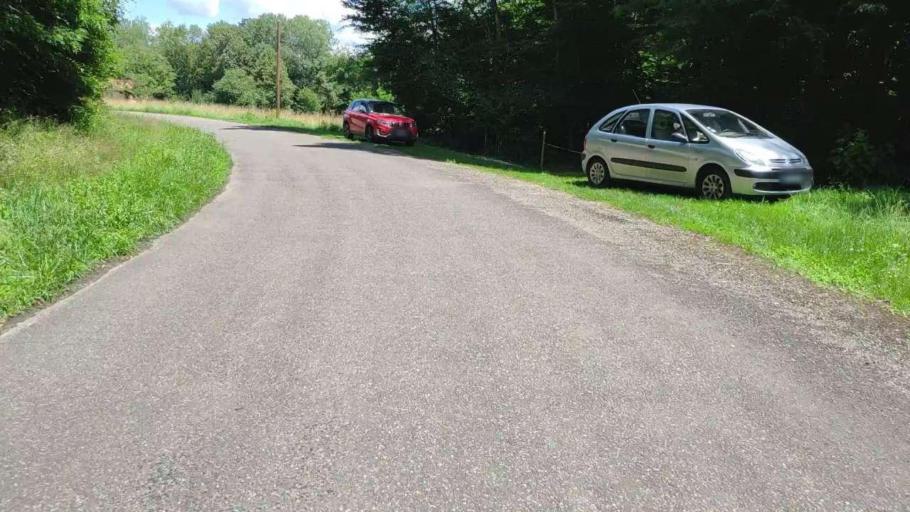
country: FR
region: Franche-Comte
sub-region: Departement du Jura
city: Chaussin
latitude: 46.8728
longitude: 5.4679
